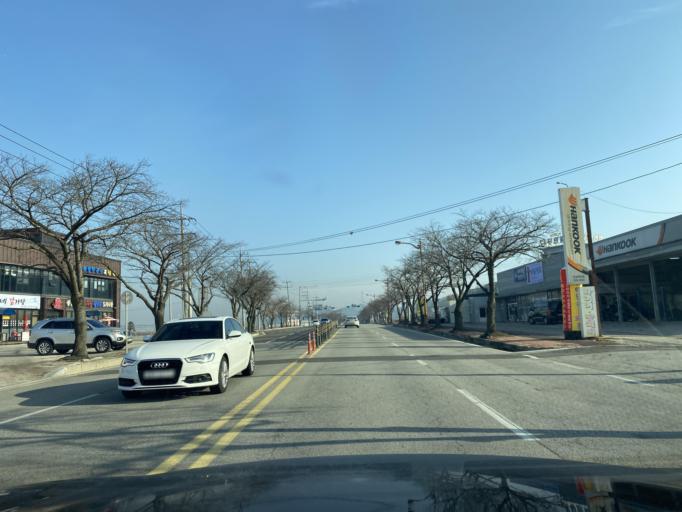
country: KR
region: Chungcheongnam-do
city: Yesan
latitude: 36.7226
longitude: 126.8491
